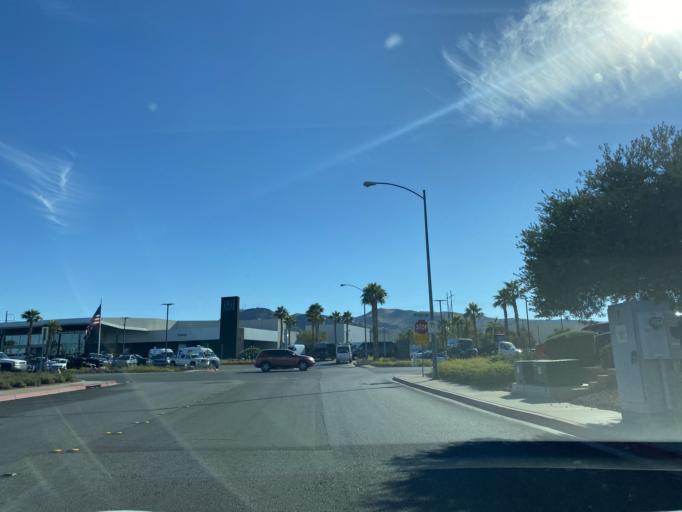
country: US
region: Nevada
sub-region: Clark County
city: Henderson
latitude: 36.0459
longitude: -115.0253
